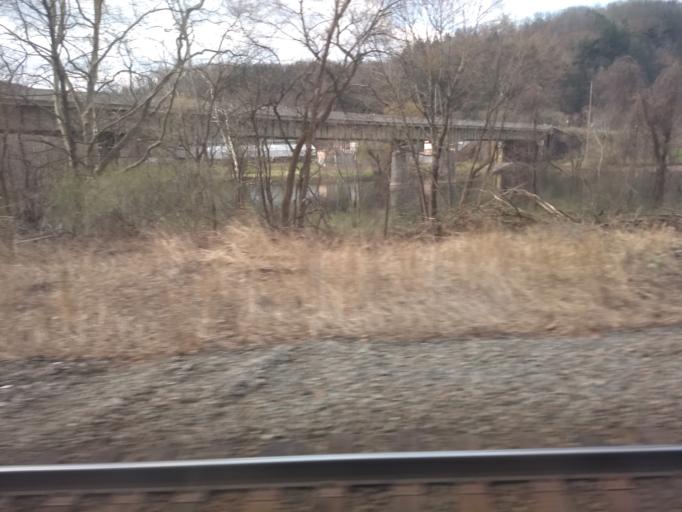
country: US
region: Pennsylvania
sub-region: Huntingdon County
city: Huntingdon
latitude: 40.4773
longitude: -78.0004
